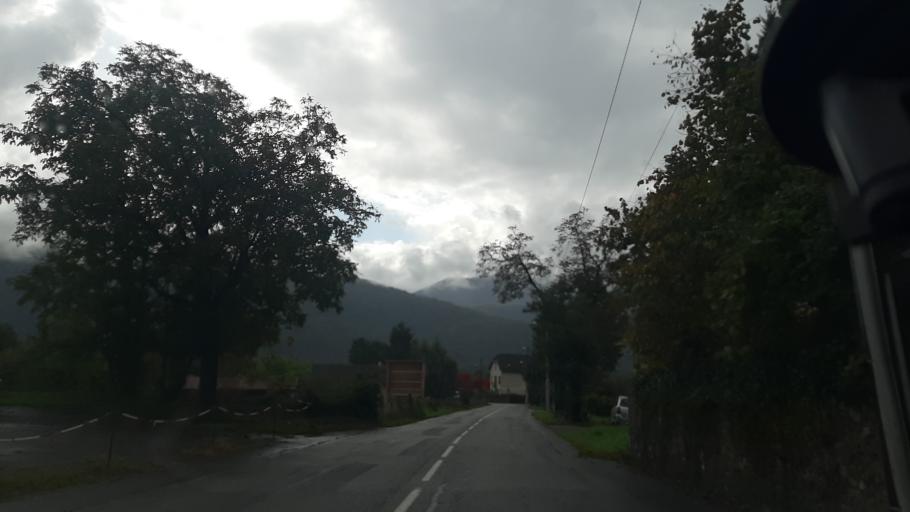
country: FR
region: Rhone-Alpes
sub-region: Departement de la Savoie
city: Gresy-sur-Isere
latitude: 45.5973
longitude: 6.2591
